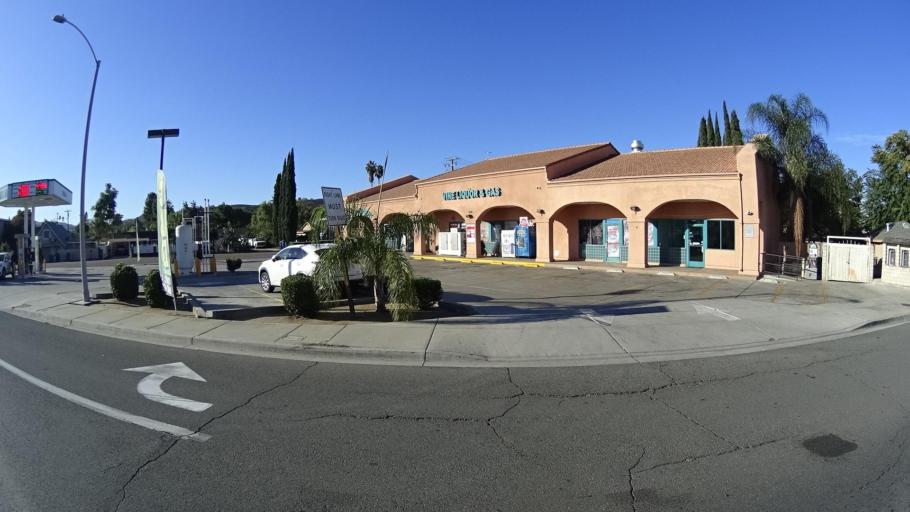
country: US
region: California
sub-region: San Diego County
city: Lakeside
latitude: 32.8558
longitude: -116.9202
